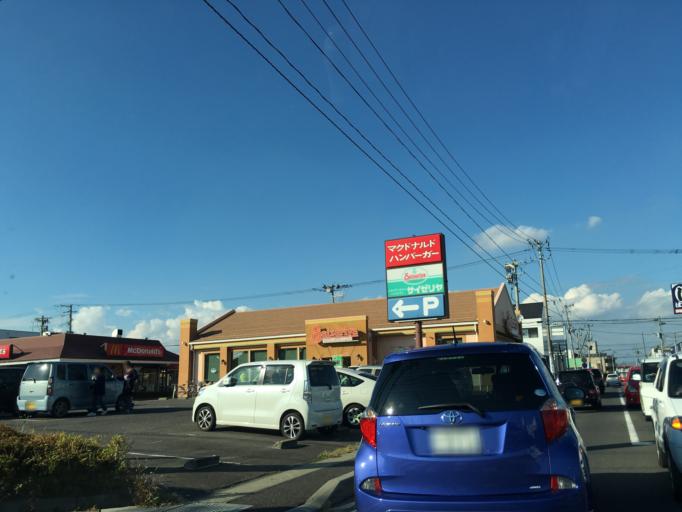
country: JP
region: Fukushima
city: Koriyama
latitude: 37.3990
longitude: 140.3340
